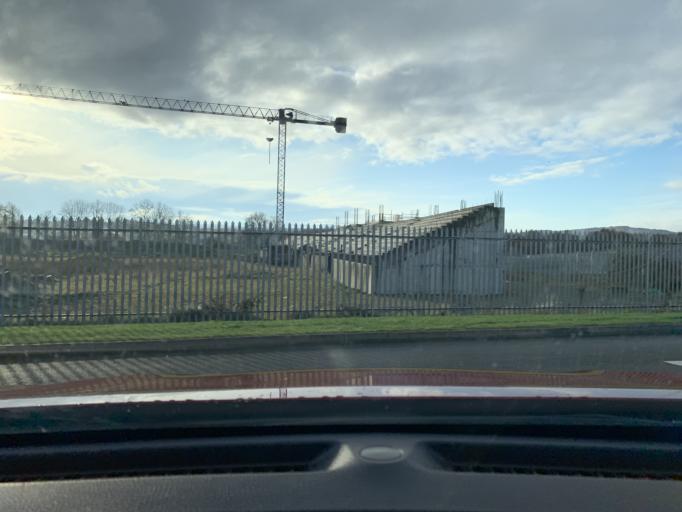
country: IE
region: Ulster
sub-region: County Donegal
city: Ballybofey
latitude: 54.8015
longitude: -7.7694
